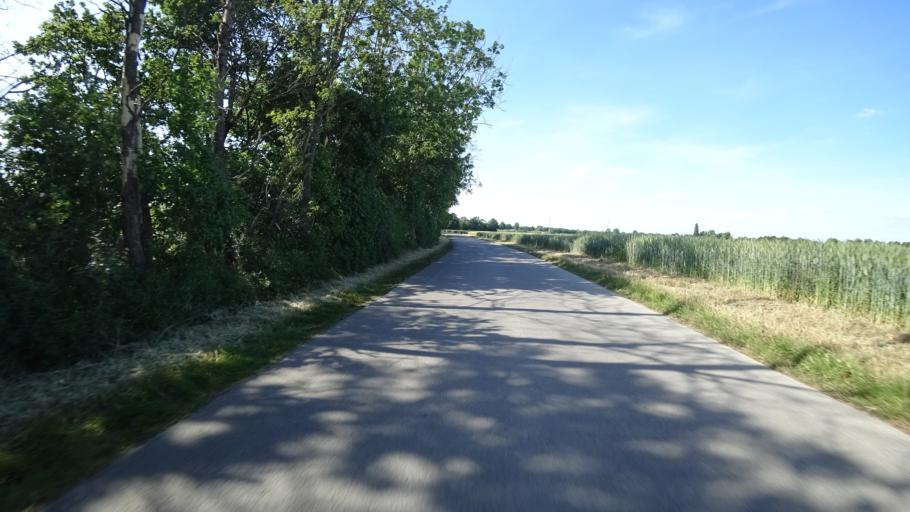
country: DE
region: North Rhine-Westphalia
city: Erwitte
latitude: 51.6135
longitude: 8.3683
